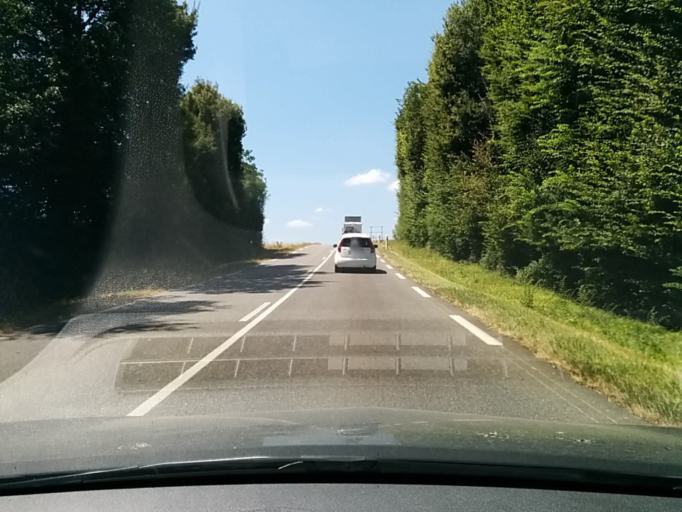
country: FR
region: Midi-Pyrenees
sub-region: Departement du Gers
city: Eauze
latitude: 43.7696
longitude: 0.1442
